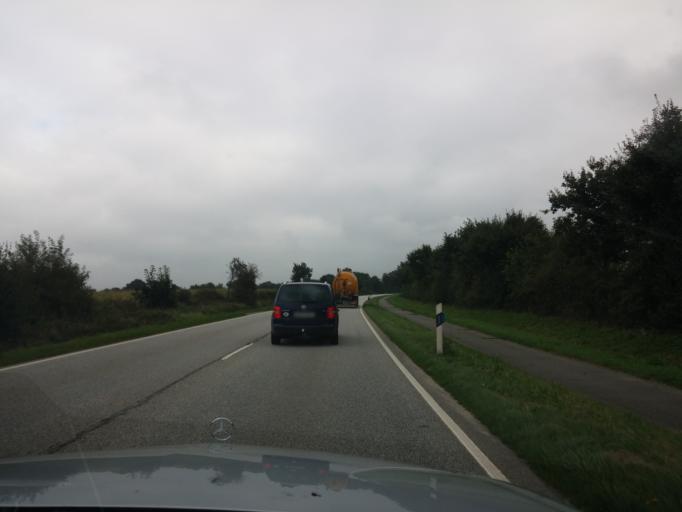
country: DE
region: Schleswig-Holstein
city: Schuby
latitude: 54.5189
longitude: 9.4532
